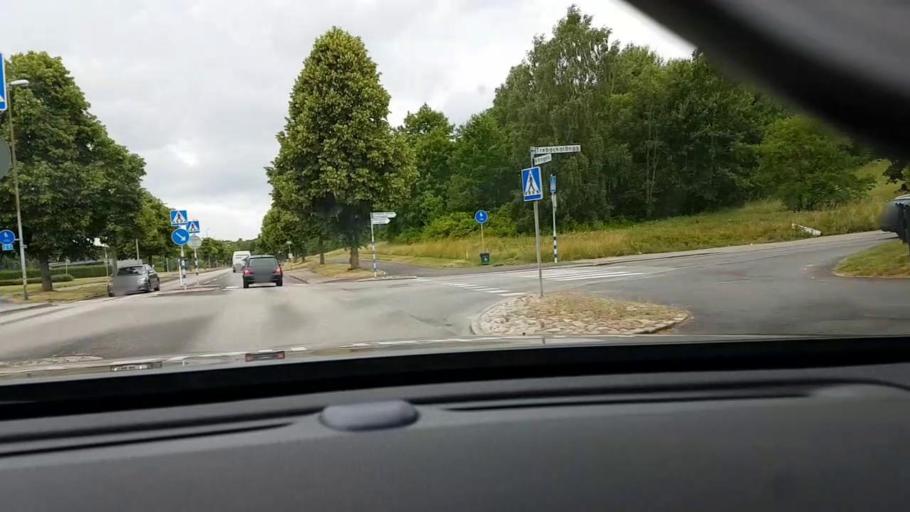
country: SE
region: Skane
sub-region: Hassleholms Kommun
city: Hassleholm
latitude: 56.1681
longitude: 13.7840
